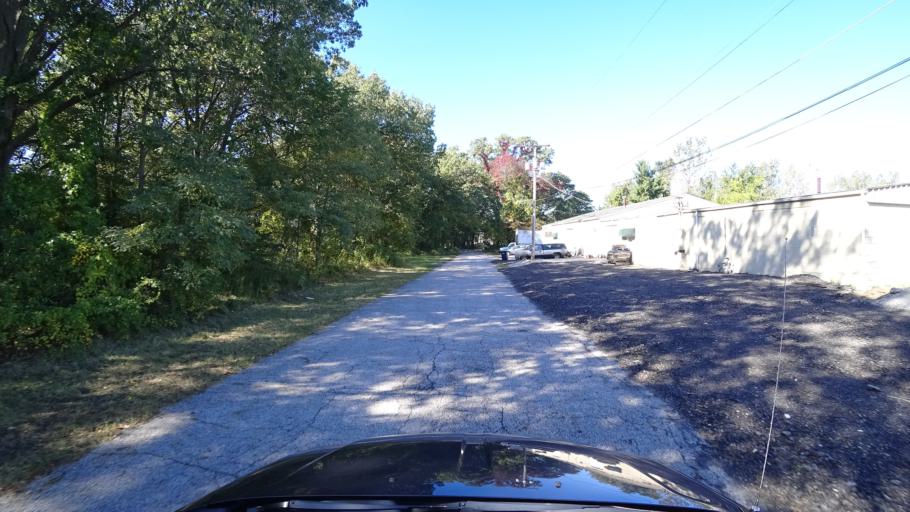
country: US
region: Indiana
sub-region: LaPorte County
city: Michigan City
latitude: 41.7012
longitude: -86.9220
